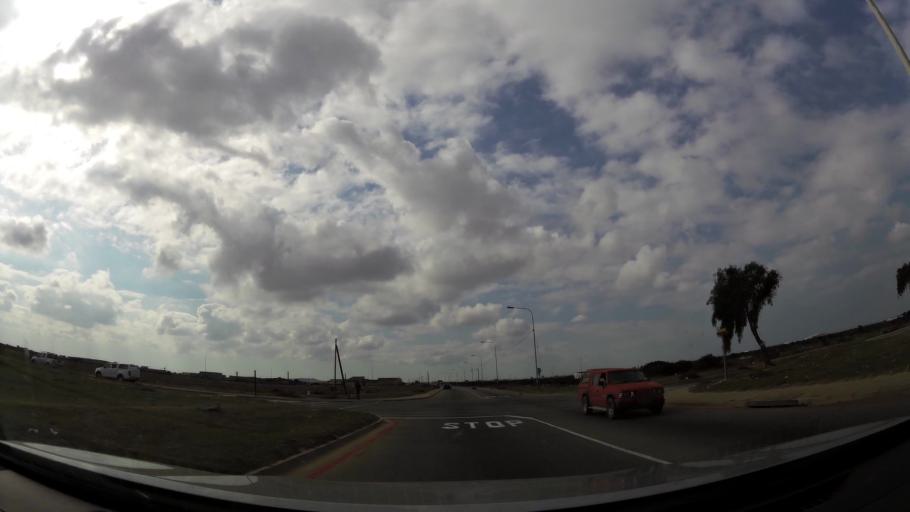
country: ZA
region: Eastern Cape
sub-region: Nelson Mandela Bay Metropolitan Municipality
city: Port Elizabeth
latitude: -33.8176
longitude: 25.5955
